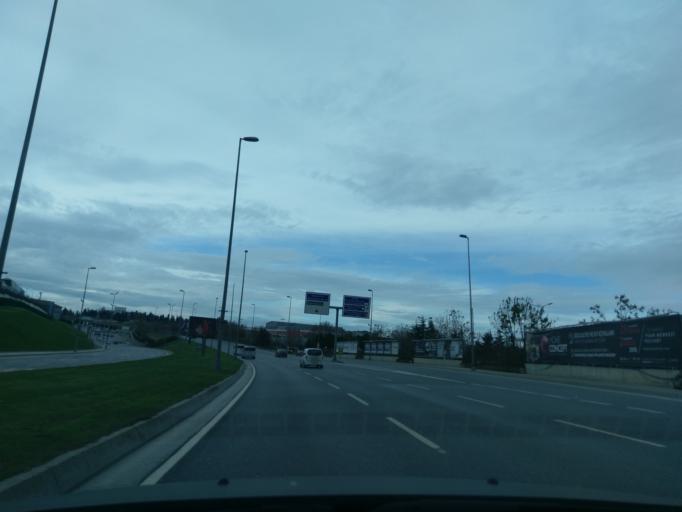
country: TR
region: Istanbul
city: Bahcelievler
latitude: 40.9850
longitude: 28.8302
